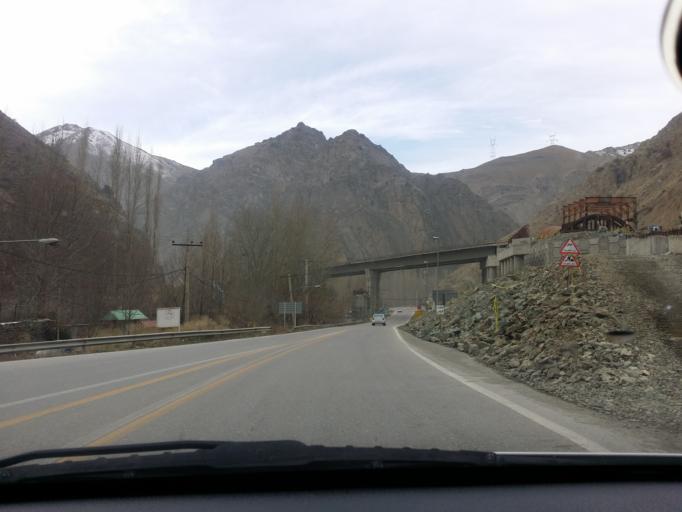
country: IR
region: Tehran
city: Tajrish
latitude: 36.0185
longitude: 51.3005
